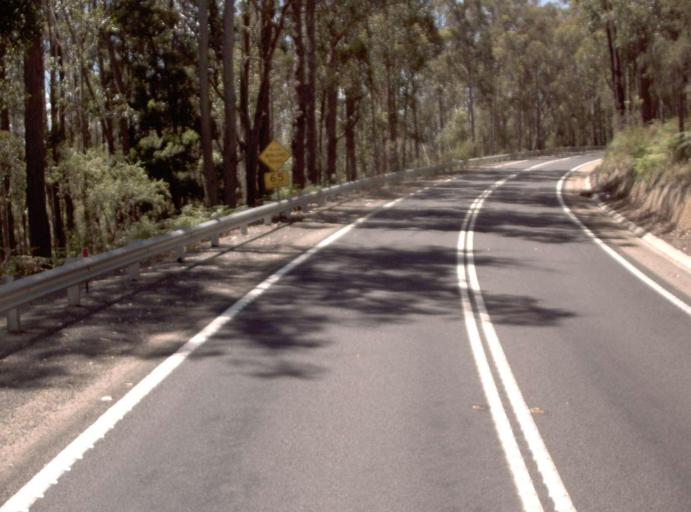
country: AU
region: Victoria
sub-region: East Gippsland
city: Lakes Entrance
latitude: -37.6953
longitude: 148.7233
